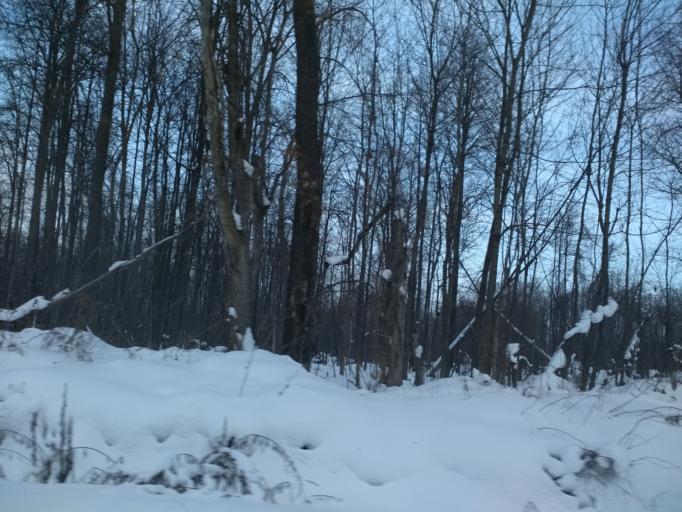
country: RU
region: Bashkortostan
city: Kudeyevskiy
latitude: 54.7142
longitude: 56.6363
